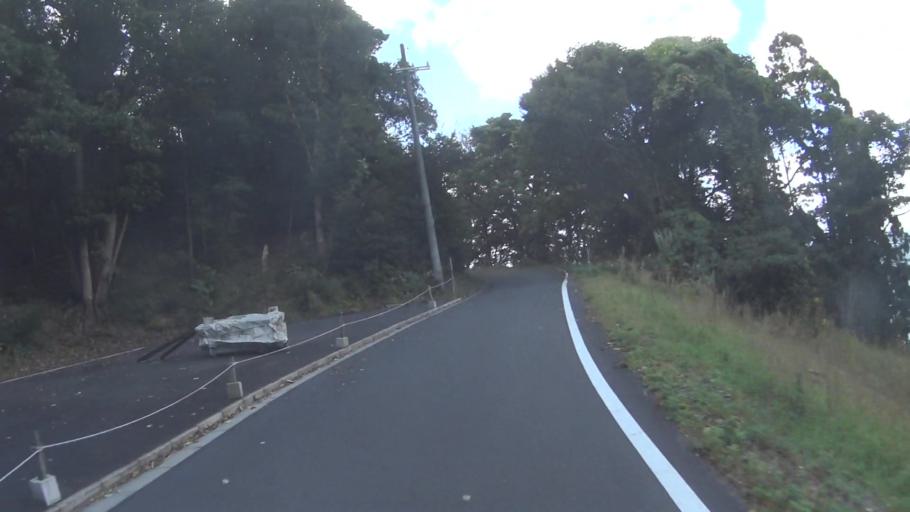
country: JP
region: Kyoto
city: Maizuru
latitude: 35.5662
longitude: 135.4221
